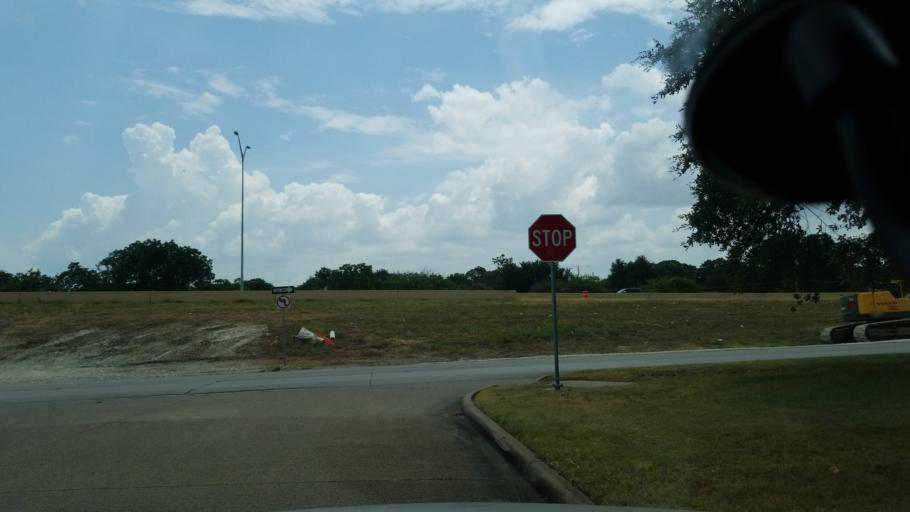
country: US
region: Texas
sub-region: Dallas County
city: Cockrell Hill
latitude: 32.6840
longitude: -96.8513
